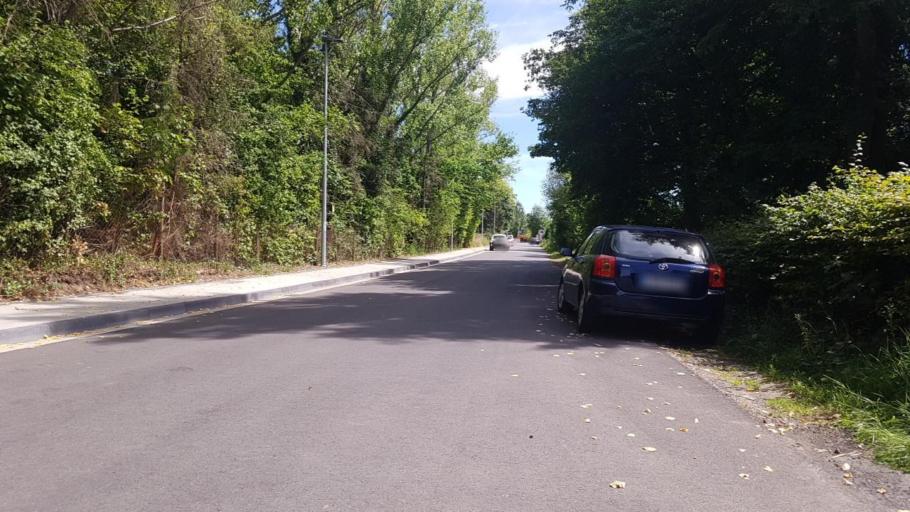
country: DE
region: North Rhine-Westphalia
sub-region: Regierungsbezirk Koln
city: Wachtberg
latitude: 50.6342
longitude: 7.0955
